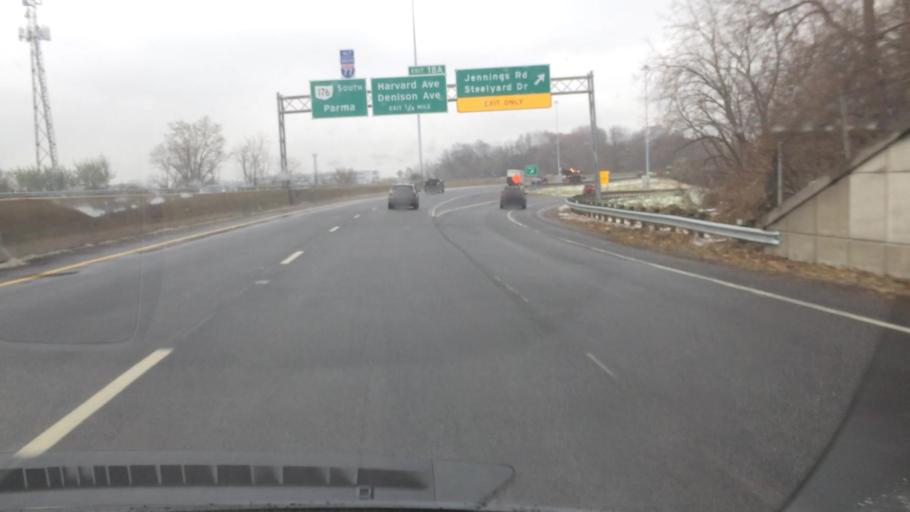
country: US
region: Ohio
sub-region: Cuyahoga County
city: Newburgh Heights
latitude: 41.4576
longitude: -81.6920
